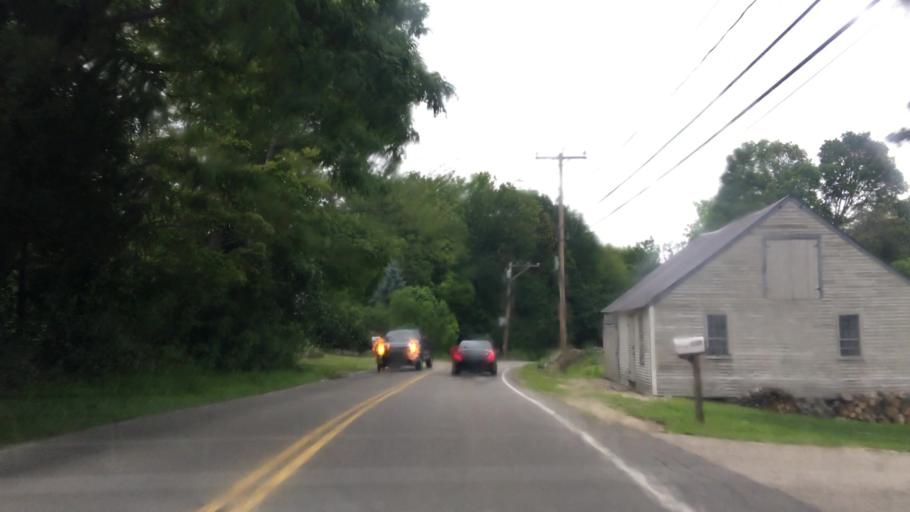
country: US
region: Maine
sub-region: York County
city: South Eliot
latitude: 43.1028
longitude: -70.8324
